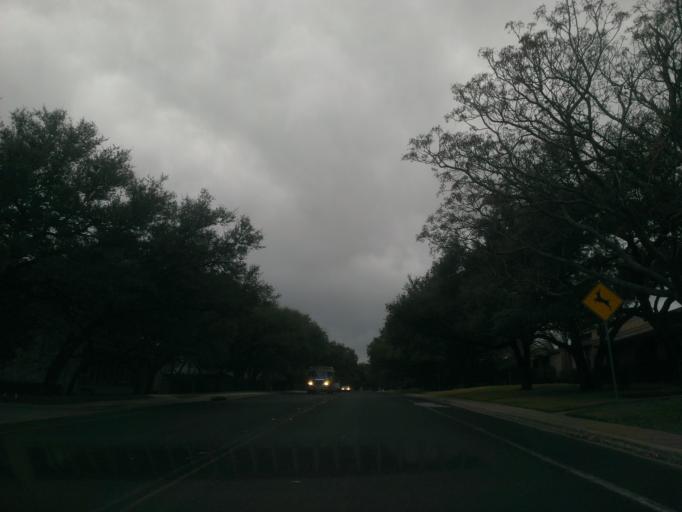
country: US
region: Texas
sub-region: Williamson County
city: Jollyville
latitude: 30.3701
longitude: -97.7580
